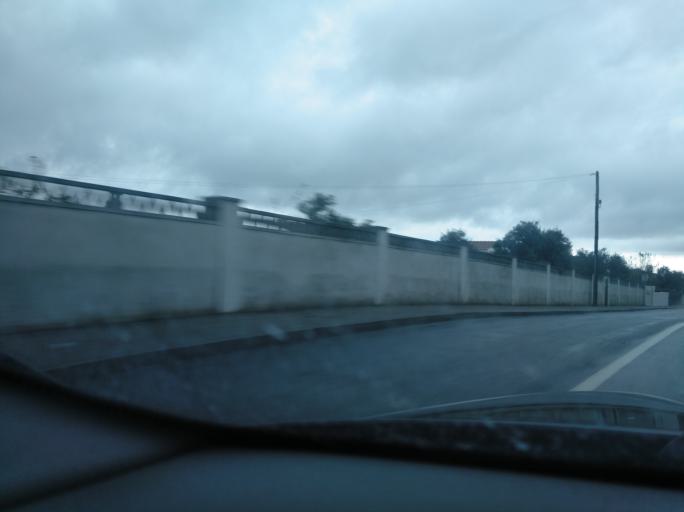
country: PT
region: Beja
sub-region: Aljustrel
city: Aljustrel
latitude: 37.8789
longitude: -8.1566
